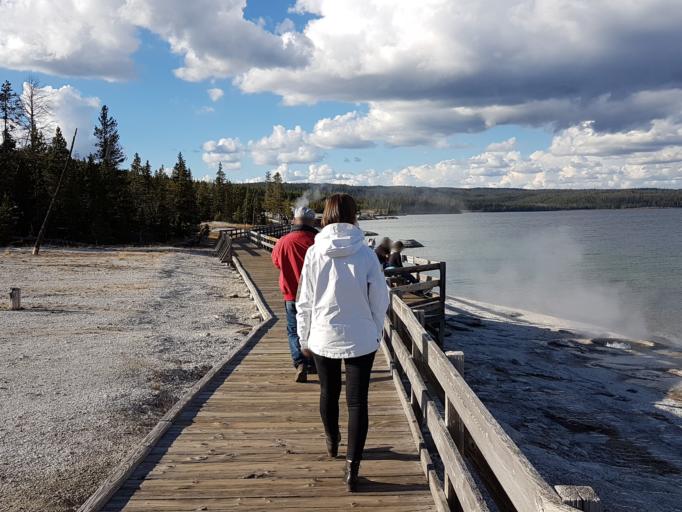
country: US
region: Montana
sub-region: Gallatin County
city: West Yellowstone
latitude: 44.4166
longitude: -110.5698
